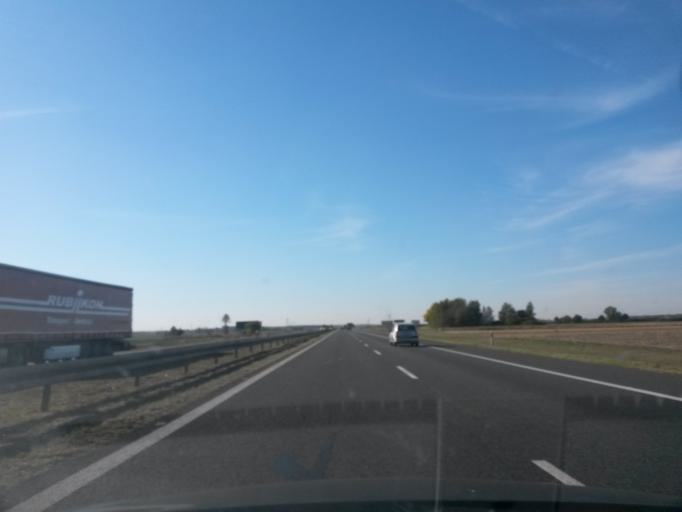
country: PL
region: Opole Voivodeship
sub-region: Powiat brzeski
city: Lewin Brzeski
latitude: 50.7106
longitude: 17.5944
